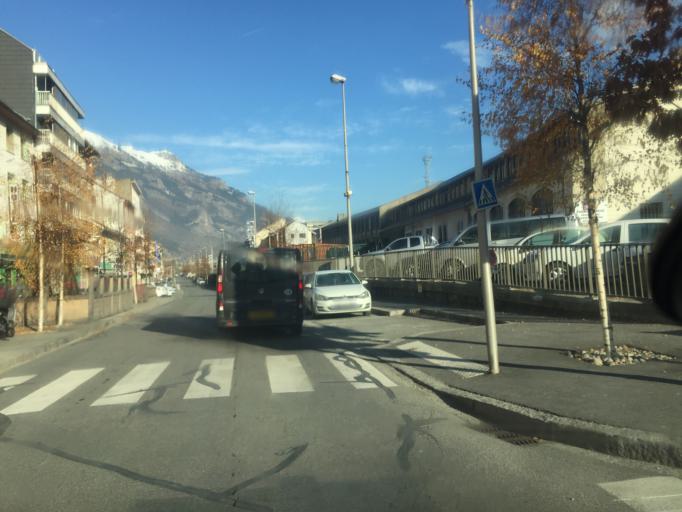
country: FR
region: Rhone-Alpes
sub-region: Departement de la Savoie
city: Modane
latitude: 45.1941
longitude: 6.6595
